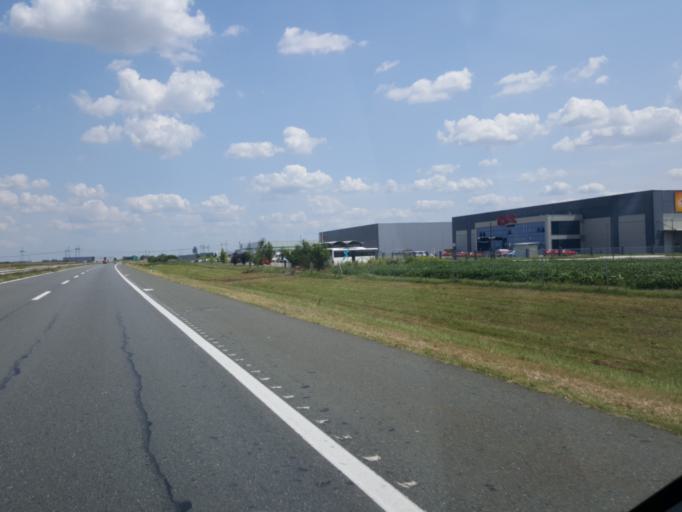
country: RS
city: Simanovci
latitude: 44.8893
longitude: 20.0935
